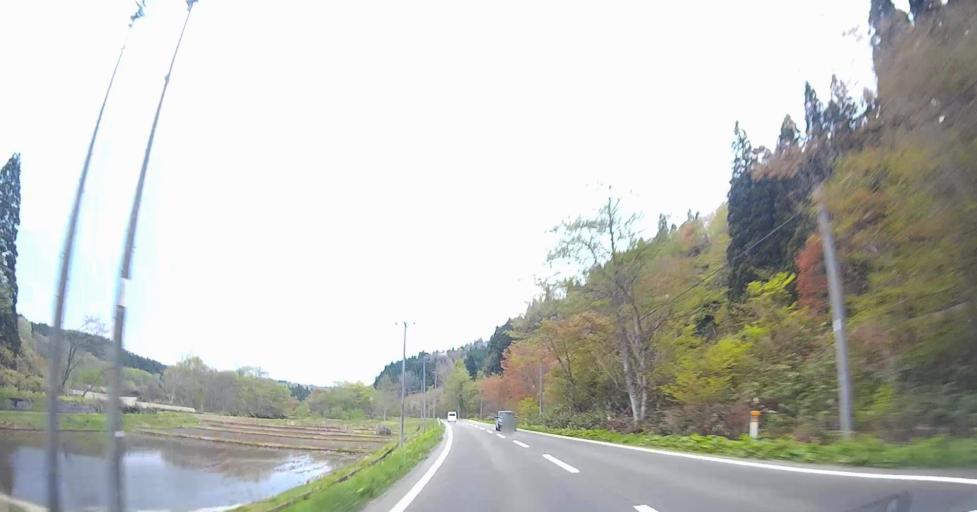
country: JP
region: Aomori
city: Goshogawara
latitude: 41.1252
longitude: 140.5196
